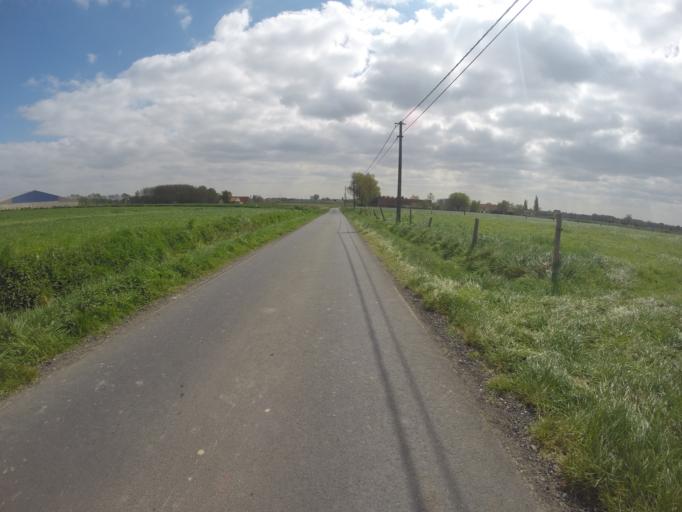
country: BE
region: Flanders
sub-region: Provincie Oost-Vlaanderen
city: Nevele
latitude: 51.0323
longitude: 3.4874
